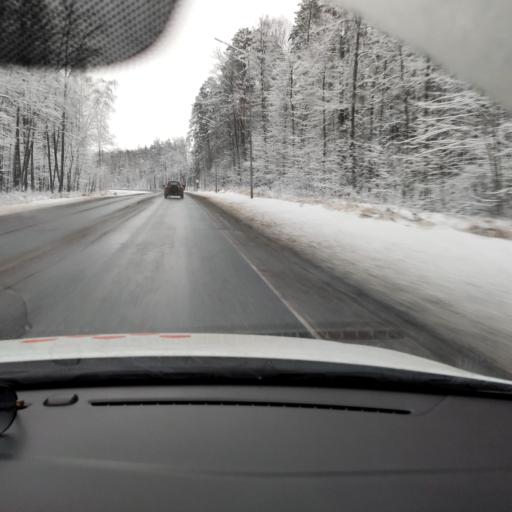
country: RU
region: Tatarstan
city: Stolbishchi
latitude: 55.6326
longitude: 49.0973
